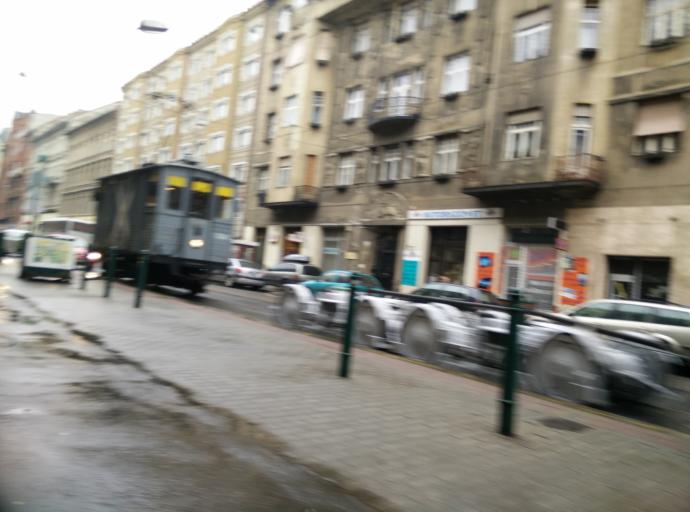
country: HU
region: Budapest
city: Budapest VIII. keruelet
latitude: 47.4947
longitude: 19.0779
